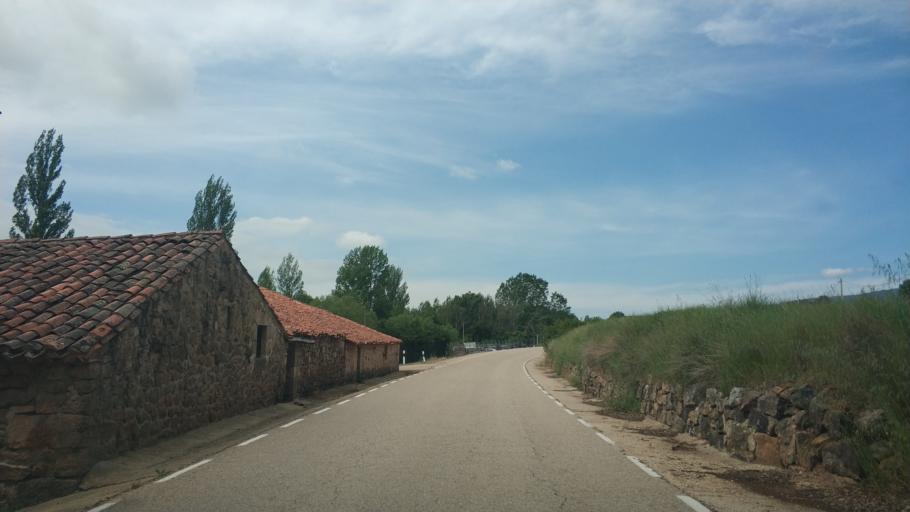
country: ES
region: Castille and Leon
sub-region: Provincia de Soria
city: Sotillo del Rincon
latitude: 41.8858
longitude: -2.6170
